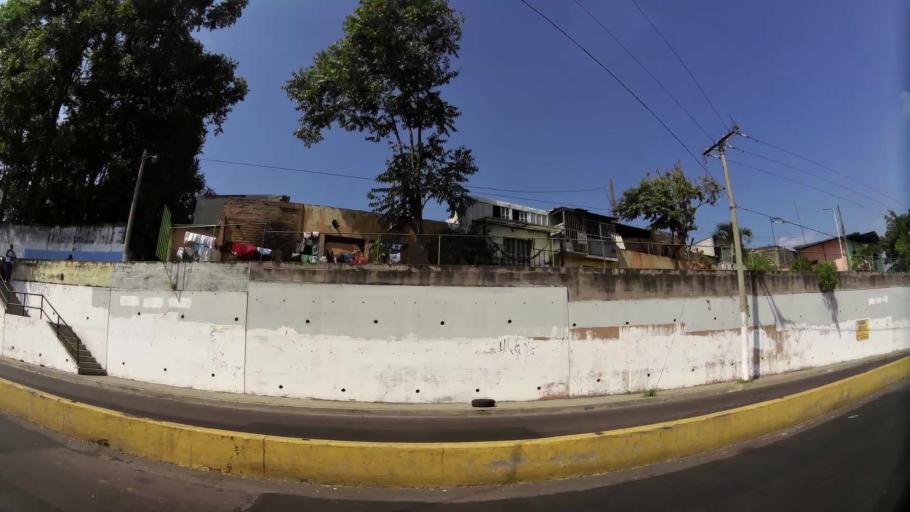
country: SV
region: San Salvador
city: San Salvador
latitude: 13.6946
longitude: -89.2216
